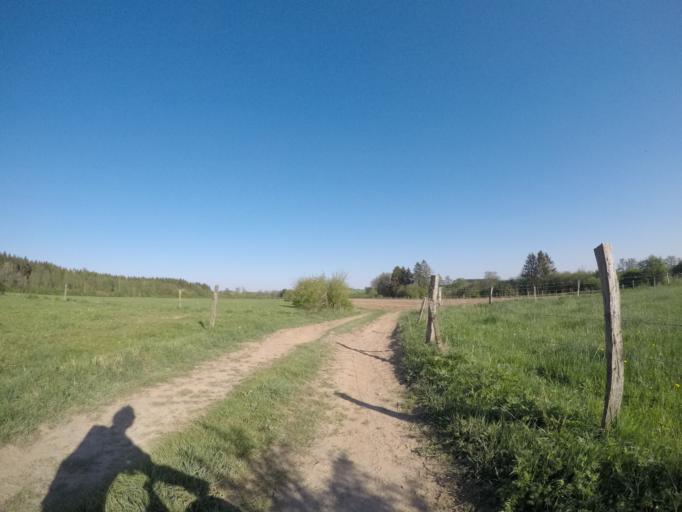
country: BE
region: Wallonia
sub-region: Province du Luxembourg
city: Tintigny
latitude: 49.7132
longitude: 5.5397
